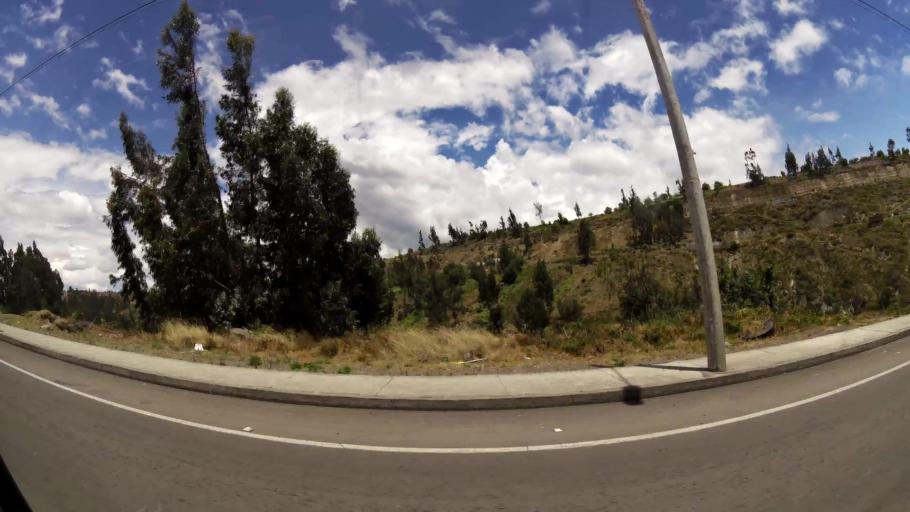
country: EC
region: Tungurahua
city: Pelileo
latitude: -1.3182
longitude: -78.5942
